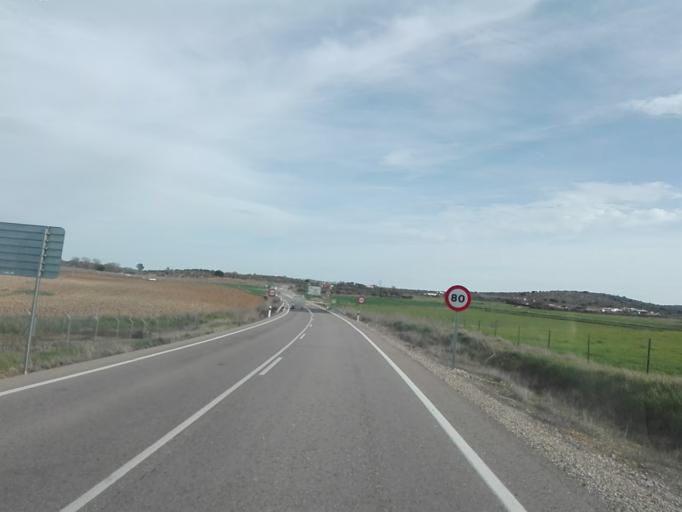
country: ES
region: Extremadura
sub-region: Provincia de Badajoz
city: Llerena
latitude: 38.2190
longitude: -6.0429
